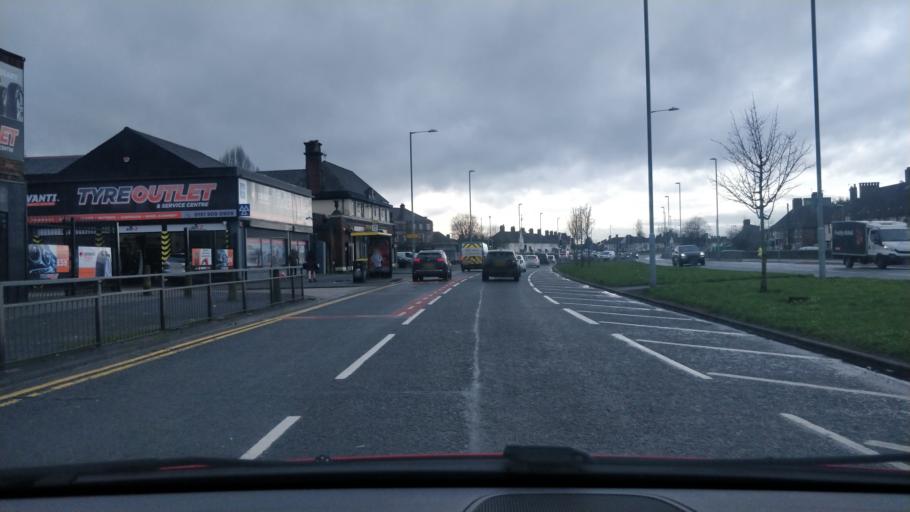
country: GB
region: England
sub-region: Knowsley
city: Huyton
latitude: 53.4202
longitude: -2.8502
